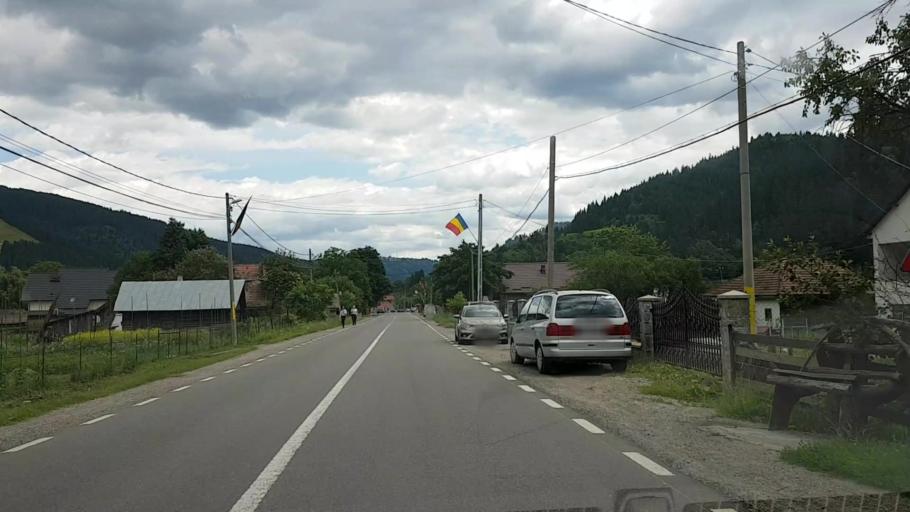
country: RO
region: Neamt
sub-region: Comuna Poiana Teiului
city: Poiana Teiului
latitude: 47.1166
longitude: 25.9204
